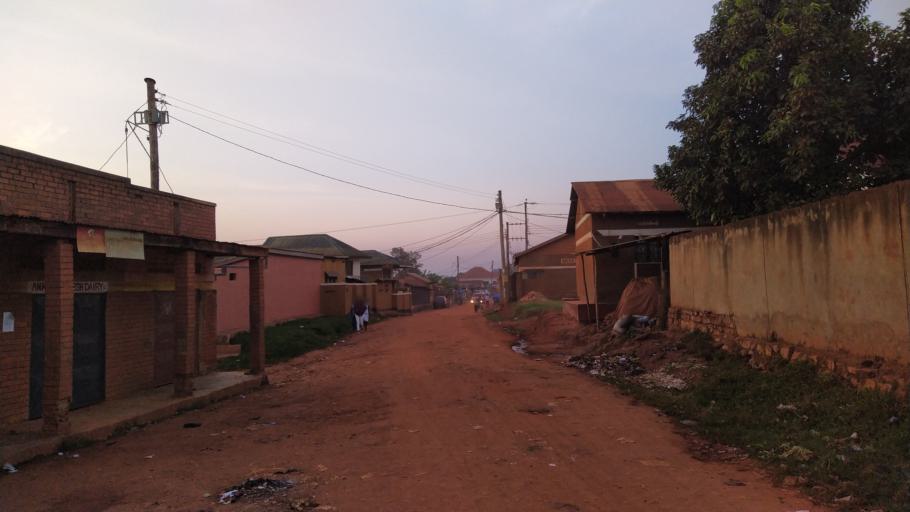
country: UG
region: Central Region
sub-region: Kampala District
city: Kampala
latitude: 0.2755
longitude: 32.5724
